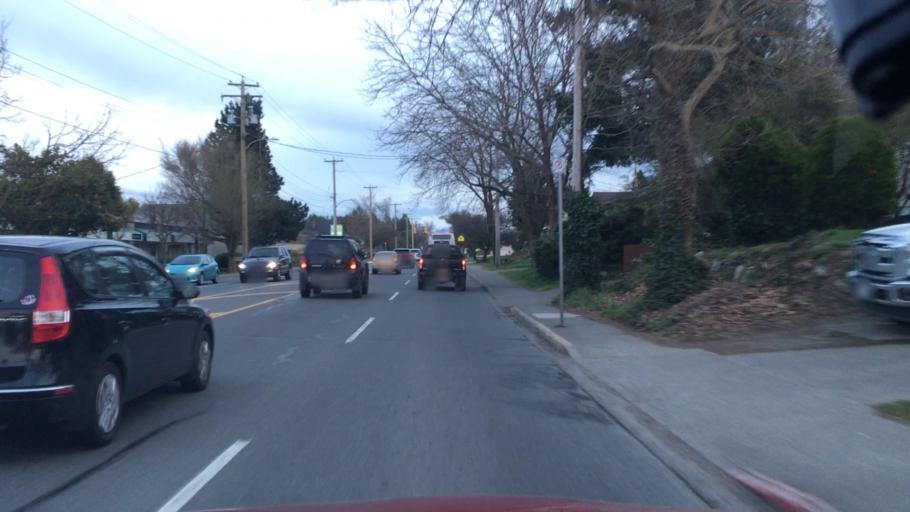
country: CA
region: British Columbia
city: Oak Bay
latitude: 48.4583
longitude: -123.3332
